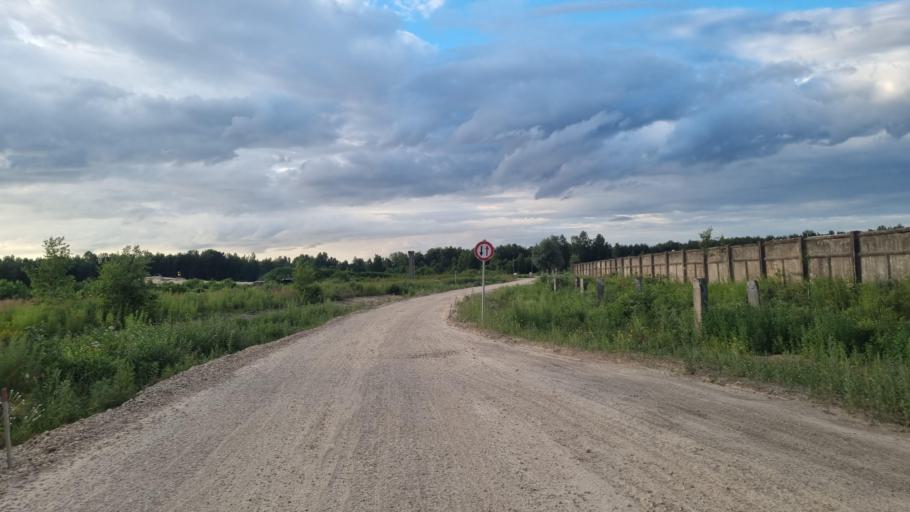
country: LV
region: Stopini
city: Ulbroka
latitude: 56.9157
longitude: 24.2390
